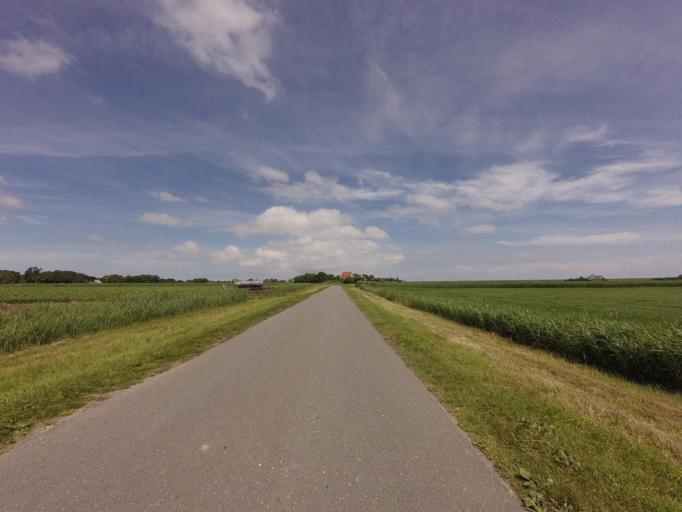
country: NL
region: North Holland
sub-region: Gemeente Texel
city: Den Burg
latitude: 53.0782
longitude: 4.8811
